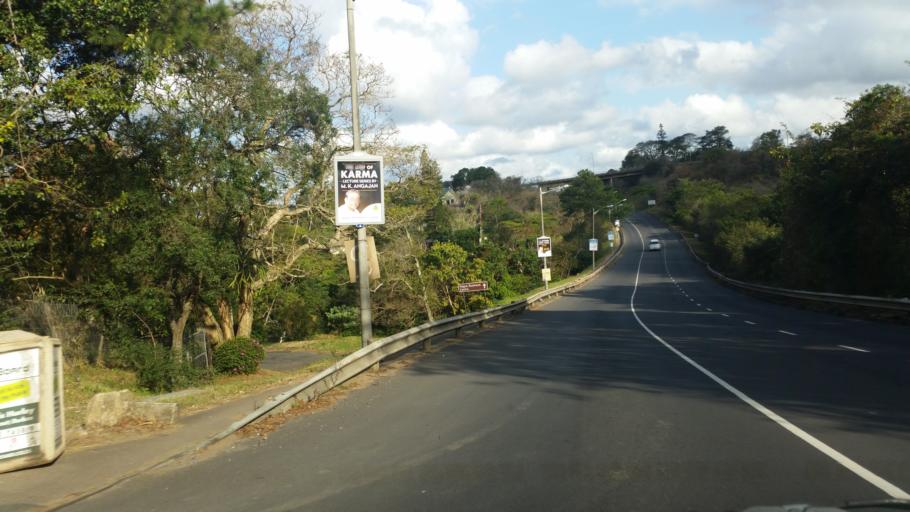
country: ZA
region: KwaZulu-Natal
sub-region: eThekwini Metropolitan Municipality
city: Berea
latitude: -29.8423
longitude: 30.9274
